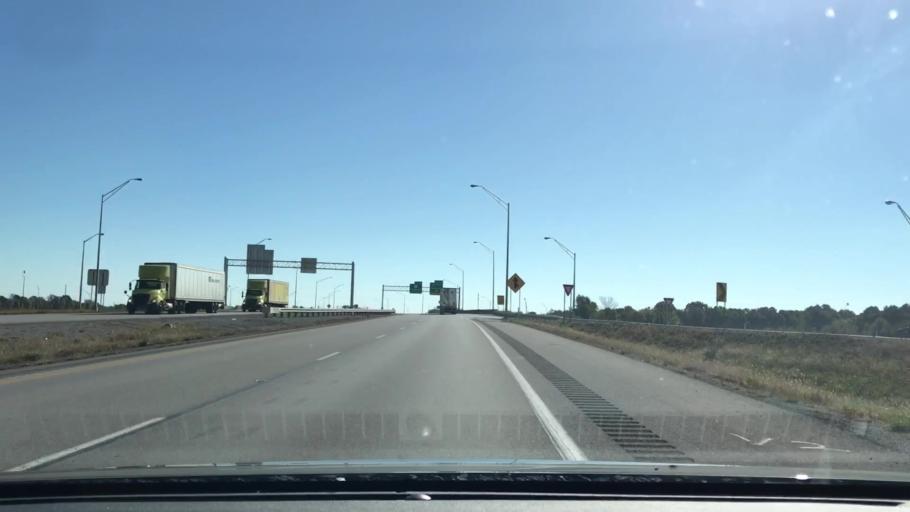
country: US
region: Kentucky
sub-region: Warren County
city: Plano
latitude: 36.9109
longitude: -86.4342
